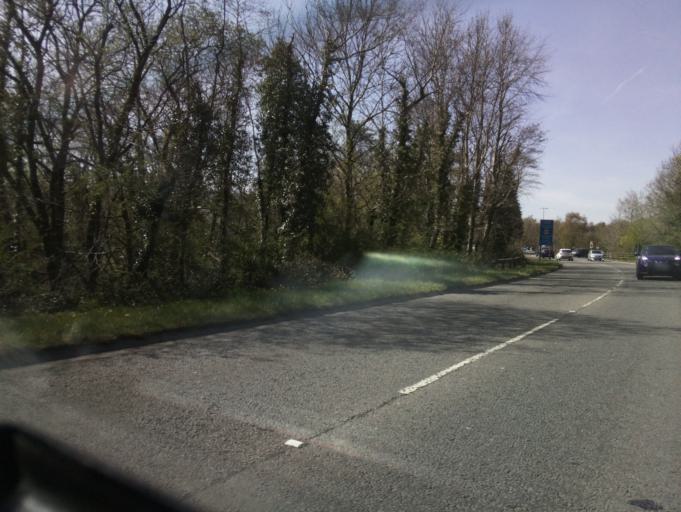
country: GB
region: Wales
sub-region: Rhondda Cynon Taf
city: Aberdare
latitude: 51.7256
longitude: -3.4564
